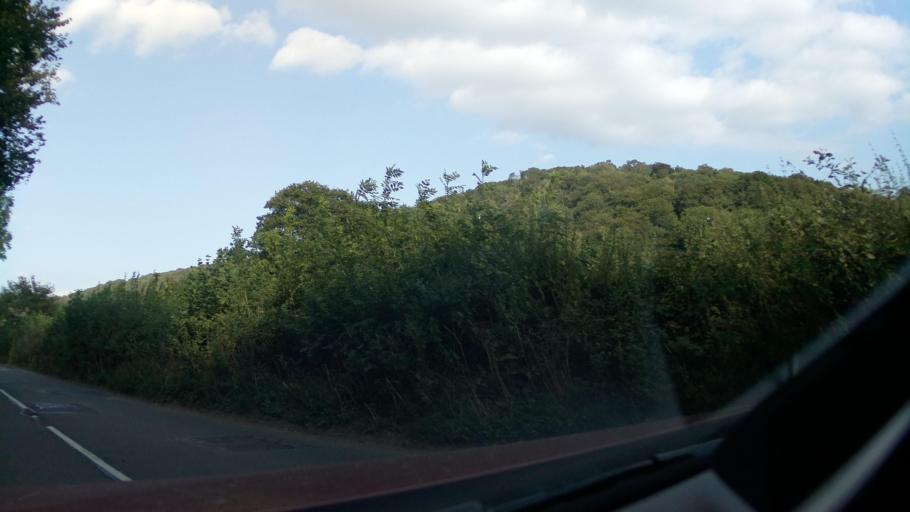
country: GB
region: England
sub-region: Devon
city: Tiverton
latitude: 50.8686
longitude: -3.4989
